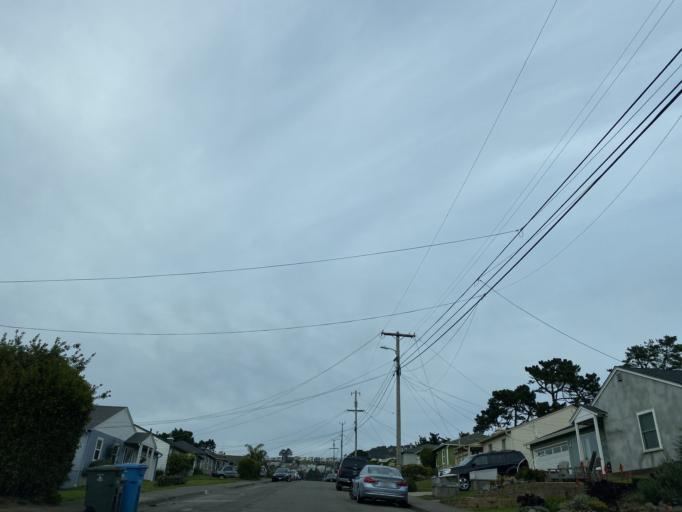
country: US
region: California
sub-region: San Mateo County
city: Pacifica
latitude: 37.6468
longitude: -122.4884
